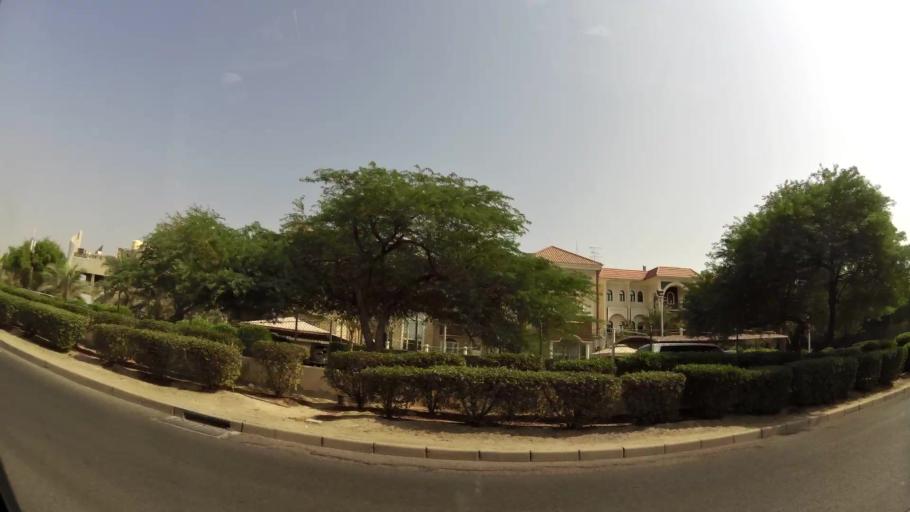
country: KW
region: Al Asimah
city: Ad Dasmah
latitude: 29.3577
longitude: 47.9894
